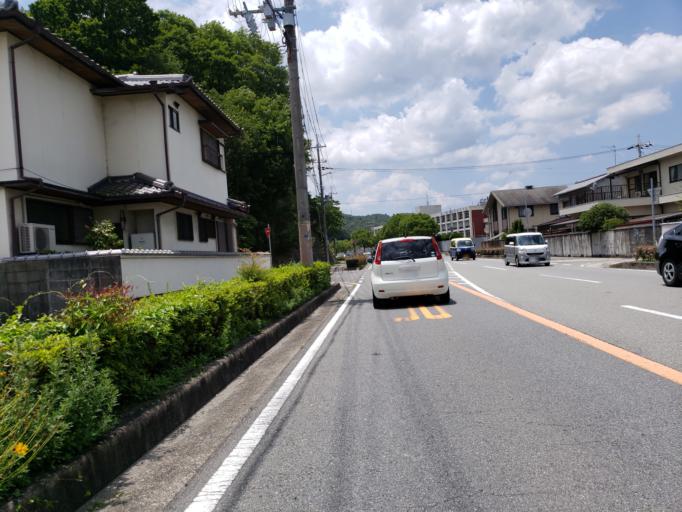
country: JP
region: Hyogo
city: Aioi
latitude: 34.8026
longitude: 134.4573
